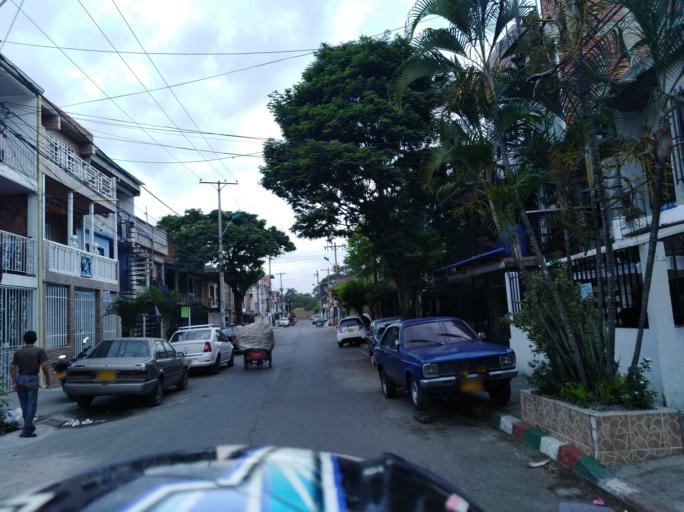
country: CO
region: Valle del Cauca
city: Cali
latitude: 3.4826
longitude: -76.4839
